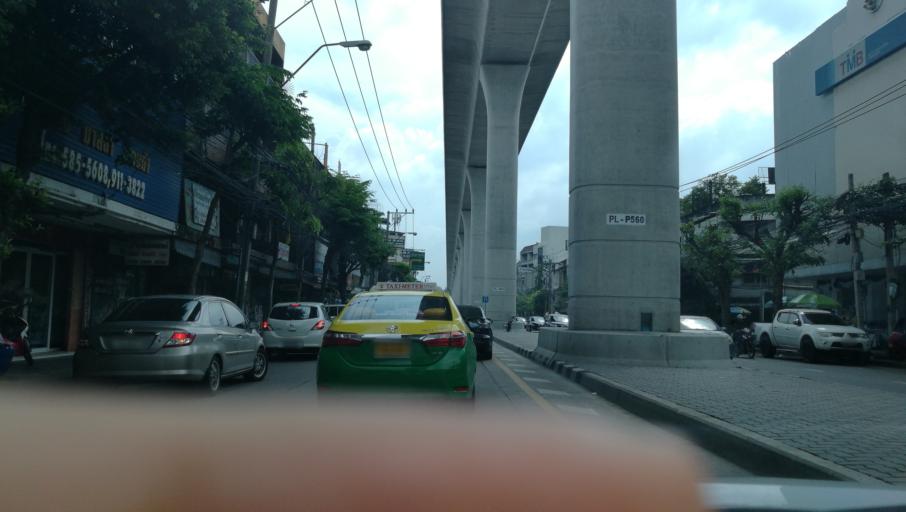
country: TH
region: Bangkok
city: Bang Sue
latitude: 13.8136
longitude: 100.5318
